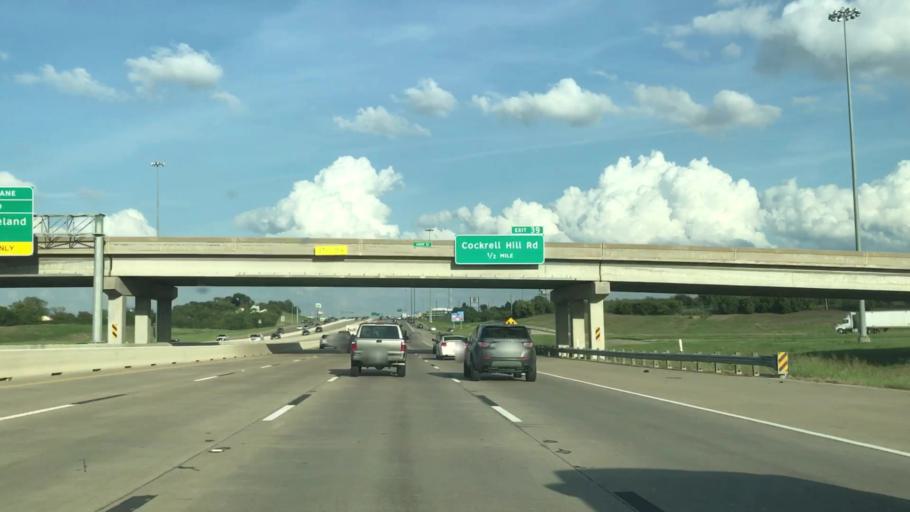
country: US
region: Texas
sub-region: Dallas County
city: Cockrell Hill
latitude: 32.7662
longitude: -96.9108
